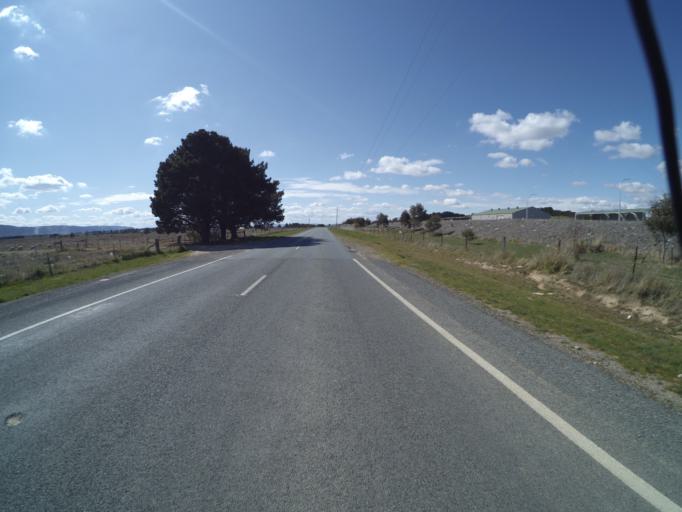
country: AU
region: New South Wales
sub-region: Palerang
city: Bungendore
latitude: -35.2374
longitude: 149.4442
